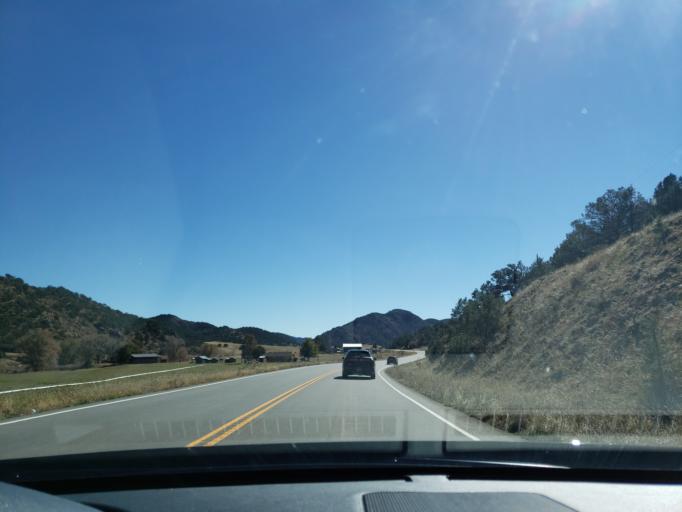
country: US
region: Colorado
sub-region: Fremont County
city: Canon City
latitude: 38.5993
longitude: -105.4285
